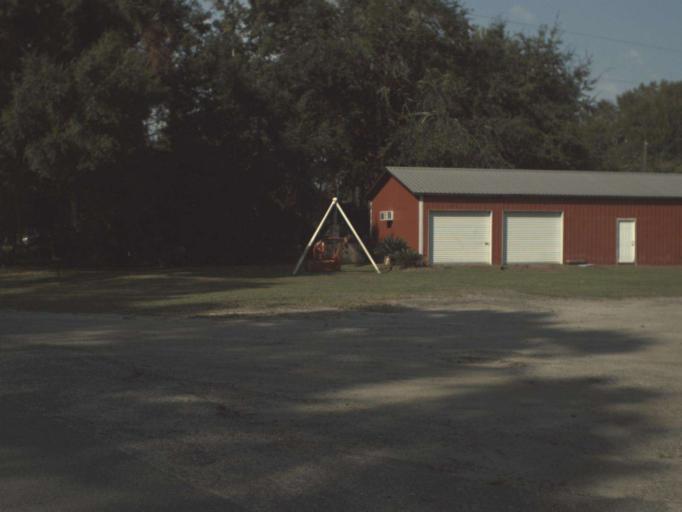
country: US
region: Florida
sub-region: Gulf County
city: Wewahitchka
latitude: 30.0940
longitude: -85.1967
